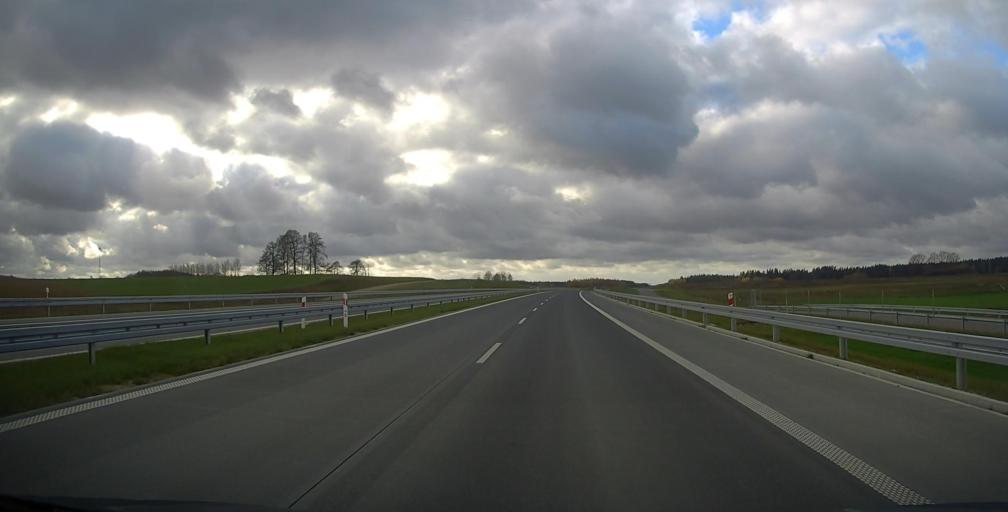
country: PL
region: Podlasie
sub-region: Powiat grajewski
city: Rajgrod
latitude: 53.8770
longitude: 22.6571
